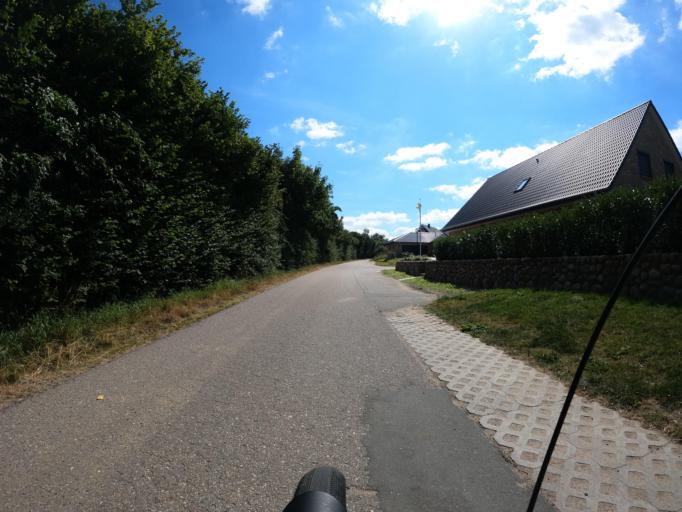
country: DE
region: Schleswig-Holstein
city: Dollerup
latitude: 54.7797
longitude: 9.6825
